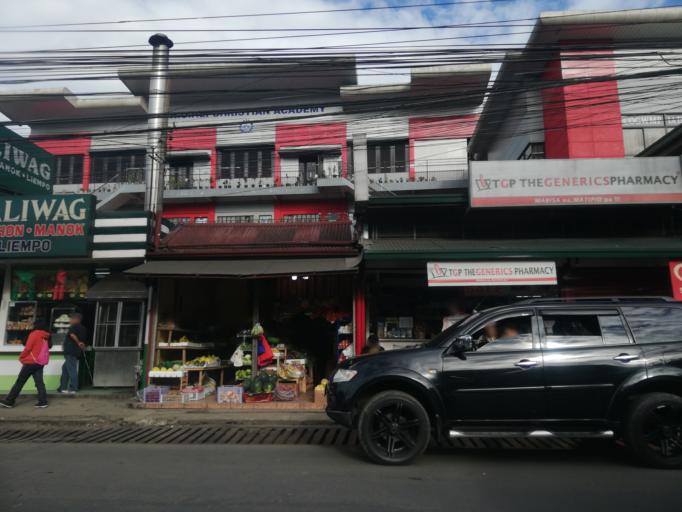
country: PH
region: Cordillera
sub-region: Province of Benguet
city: La Trinidad
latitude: 16.4466
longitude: 120.5911
